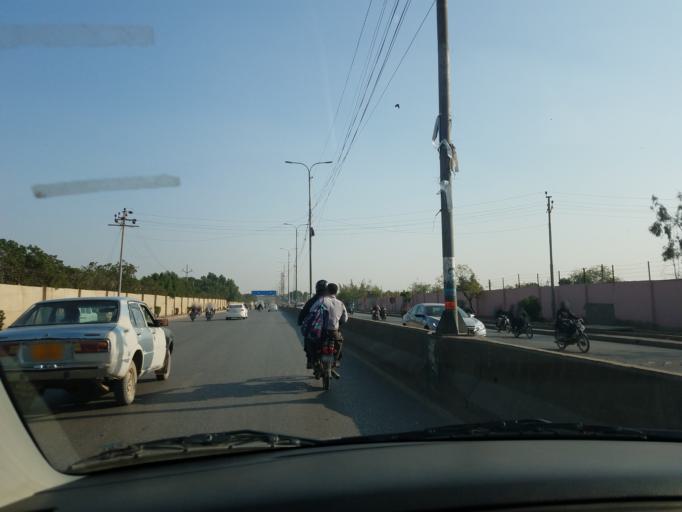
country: PK
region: Sindh
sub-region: Karachi District
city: Karachi
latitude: 24.8915
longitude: 67.1222
